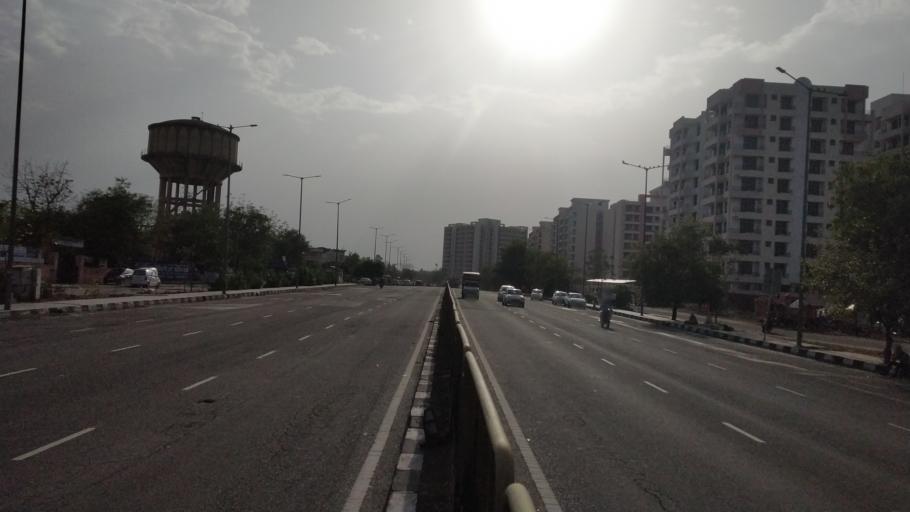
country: IN
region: Rajasthan
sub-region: Jaipur
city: Jaipur
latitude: 26.8402
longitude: 75.7743
